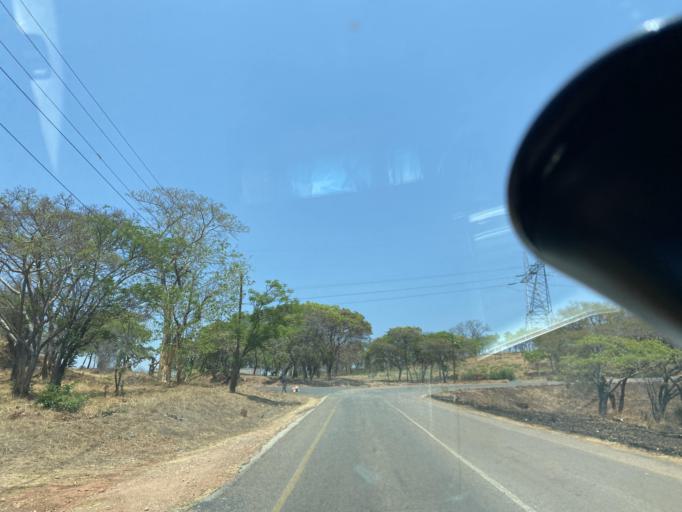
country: ZM
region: Lusaka
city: Kafue
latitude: -15.8660
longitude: 28.4580
